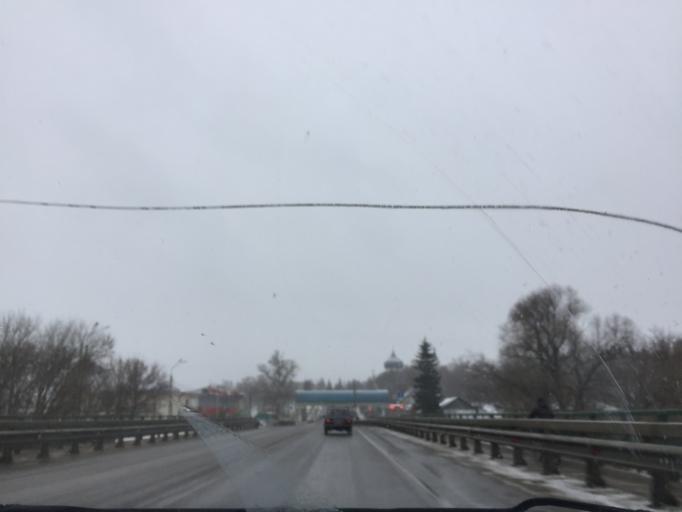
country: RU
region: Tula
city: Plavsk
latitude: 53.7120
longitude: 37.2958
